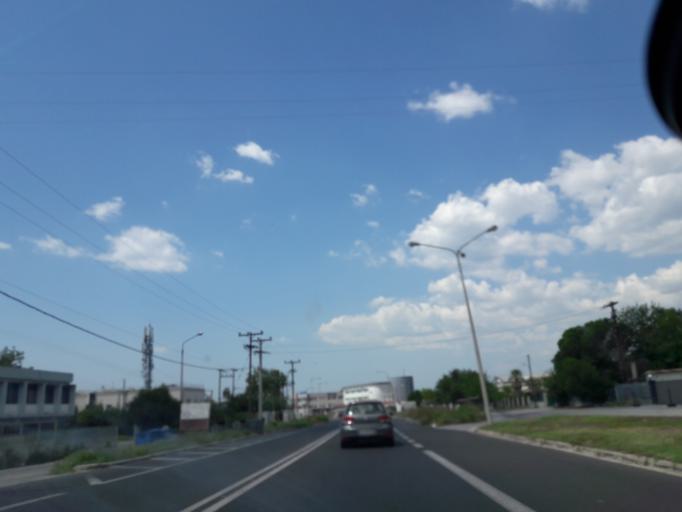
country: GR
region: Central Macedonia
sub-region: Nomos Thessalonikis
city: Thermi
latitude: 40.5403
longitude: 23.0295
